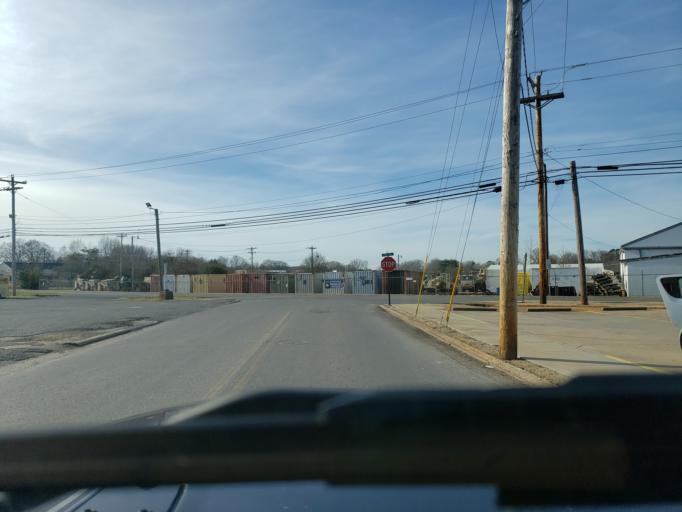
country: US
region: North Carolina
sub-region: Cleveland County
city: Kings Mountain
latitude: 35.2383
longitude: -81.3605
